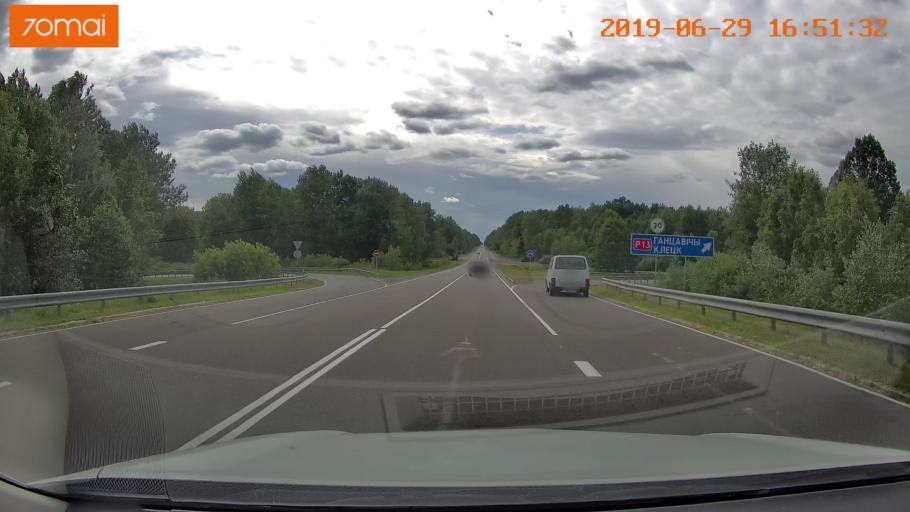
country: BY
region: Brest
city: Luninyets
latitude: 52.2813
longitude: 26.8234
